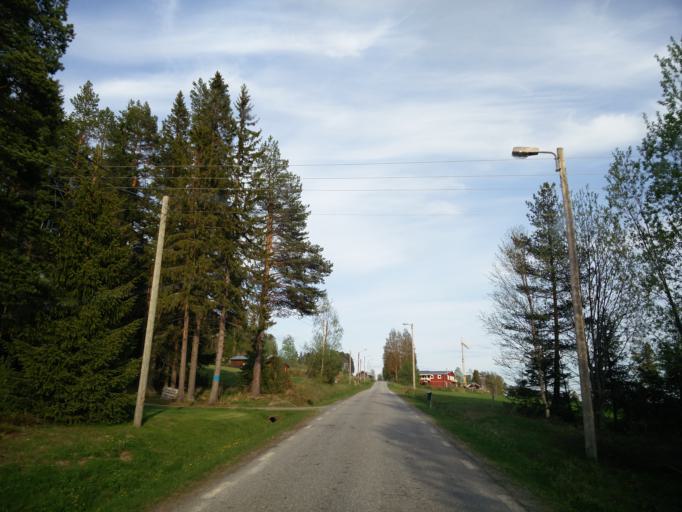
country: SE
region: Jaemtland
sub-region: Bergs Kommun
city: Hoverberg
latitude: 62.5651
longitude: 14.3762
